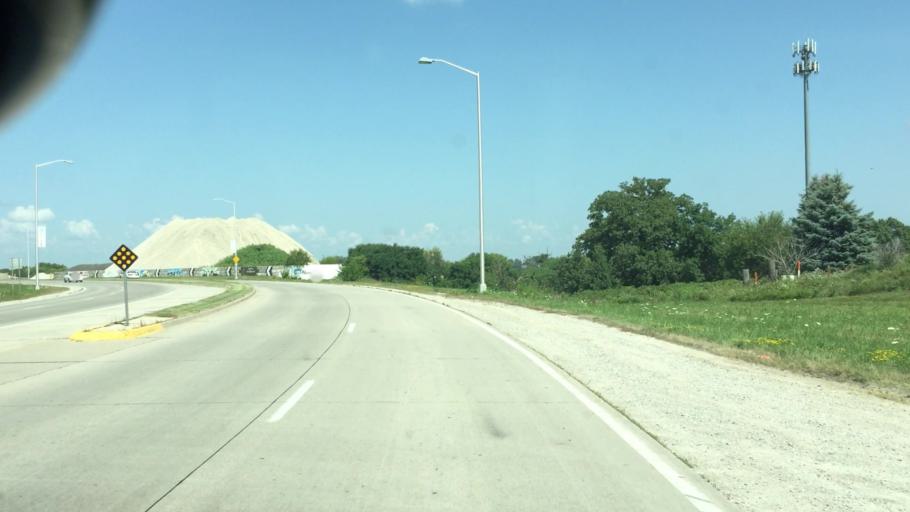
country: US
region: Iowa
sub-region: Jasper County
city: Newton
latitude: 41.6856
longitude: -93.0000
